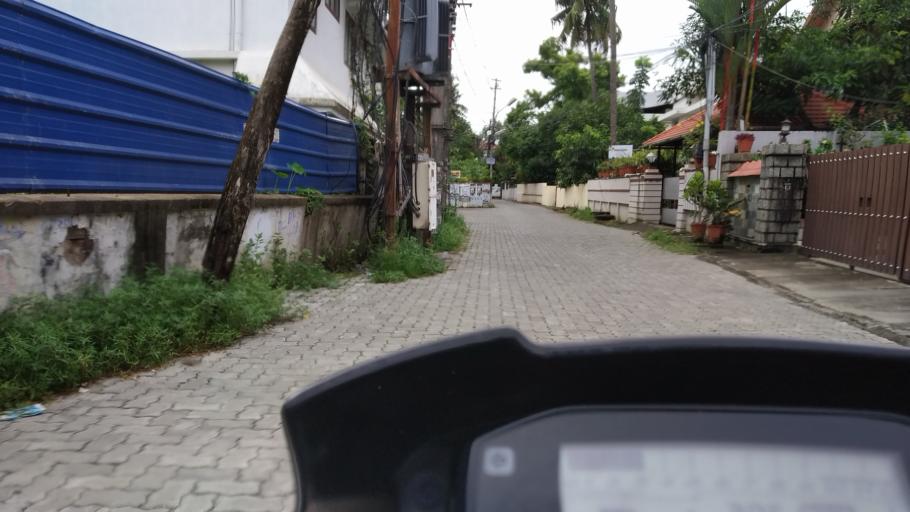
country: IN
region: Kerala
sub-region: Ernakulam
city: Cochin
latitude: 9.9934
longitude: 76.2942
